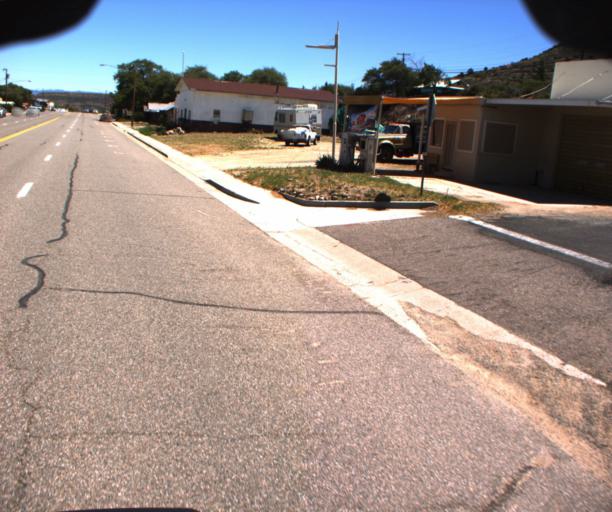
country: US
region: Arizona
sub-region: Yavapai County
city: Congress
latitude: 34.2205
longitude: -112.7481
